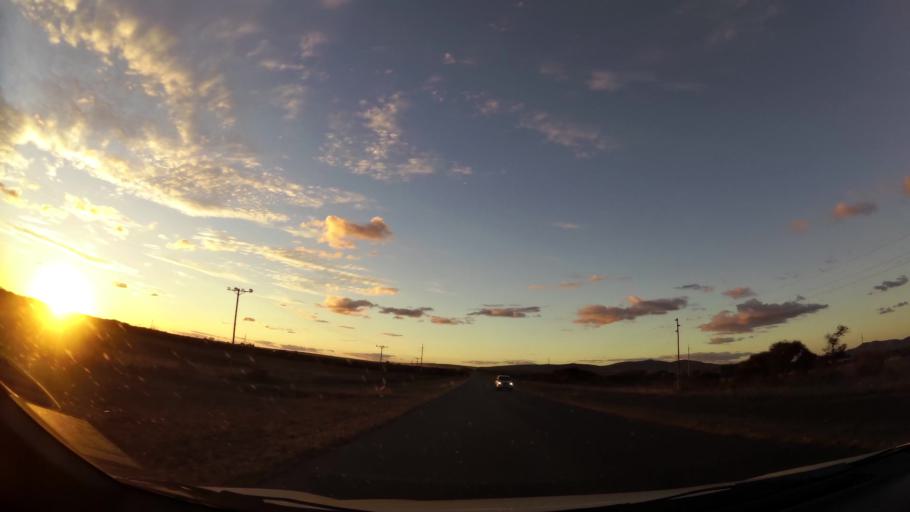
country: ZA
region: Limpopo
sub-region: Capricorn District Municipality
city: Polokwane
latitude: -23.7517
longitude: 29.4720
